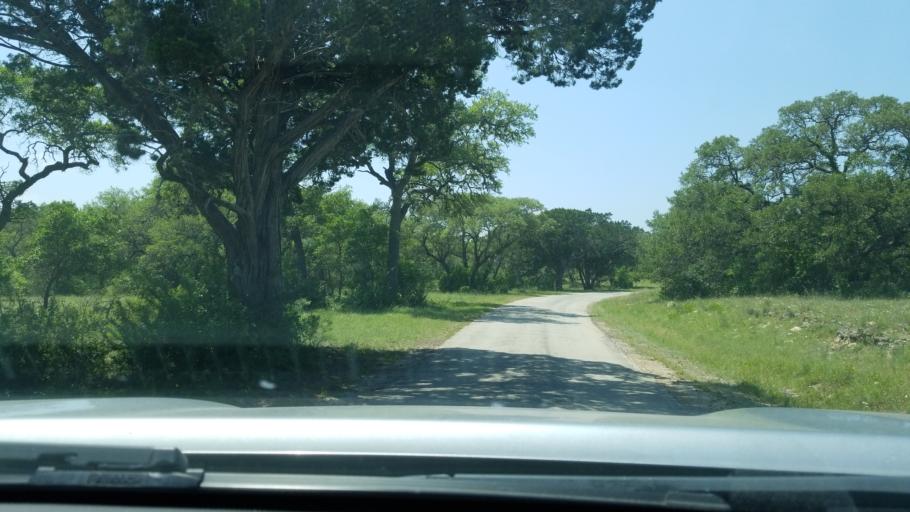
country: US
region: Texas
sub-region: Blanco County
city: Blanco
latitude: 30.0130
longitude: -98.4423
